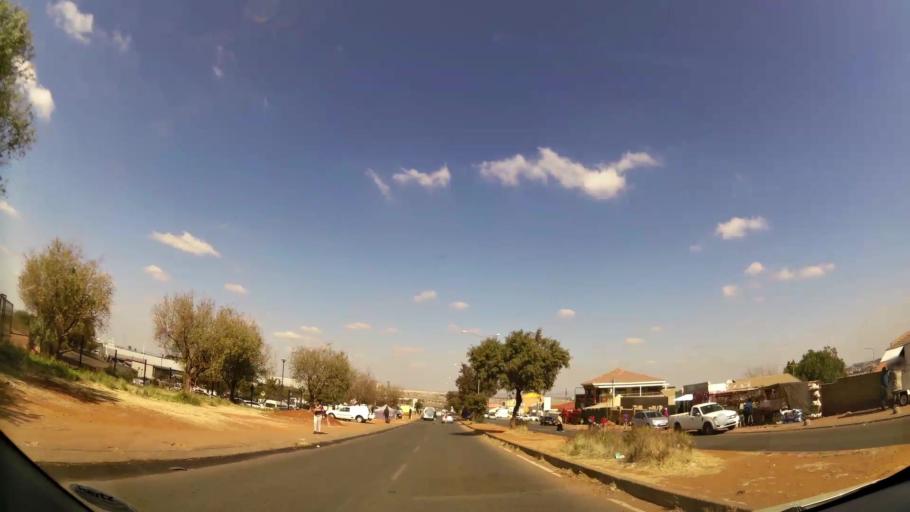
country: ZA
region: Gauteng
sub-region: West Rand District Municipality
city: Krugersdorp
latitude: -26.1649
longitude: 27.7796
